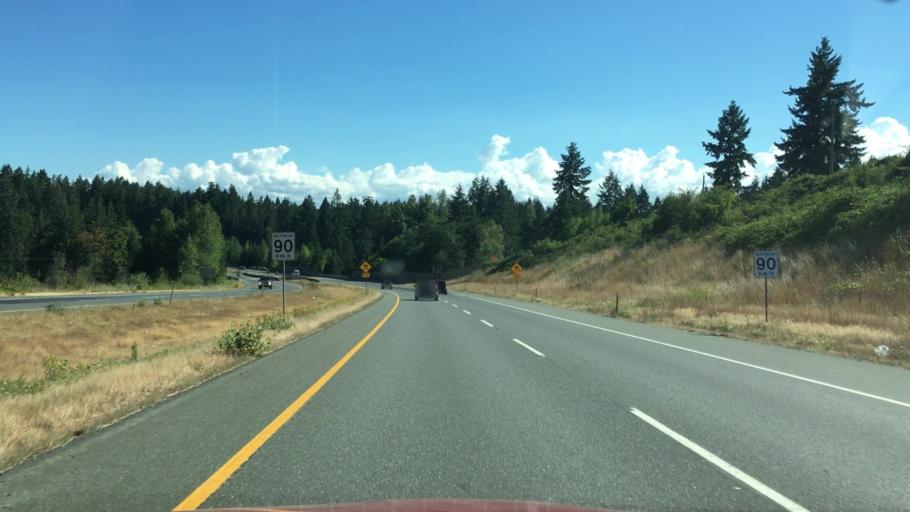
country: CA
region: British Columbia
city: Nanaimo
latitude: 49.1490
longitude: -123.9729
